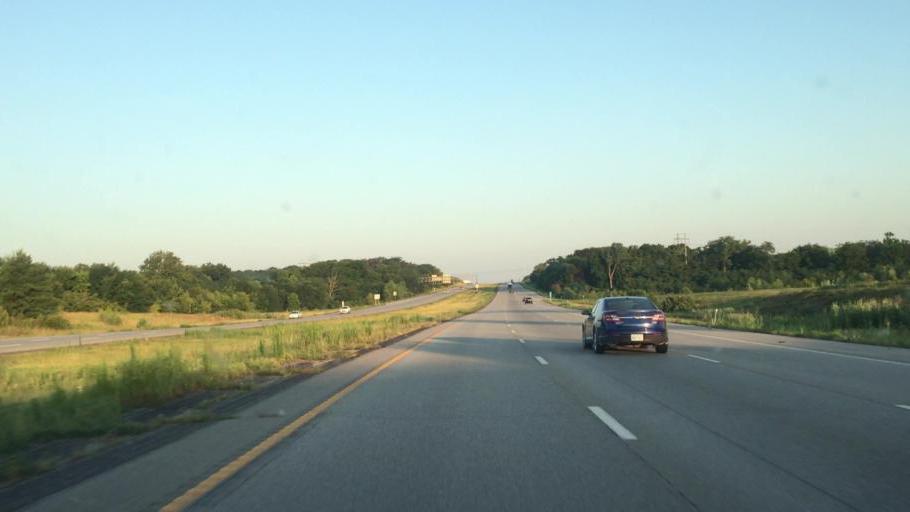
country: US
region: Missouri
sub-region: Clay County
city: Smithville
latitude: 39.3072
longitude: -94.6036
